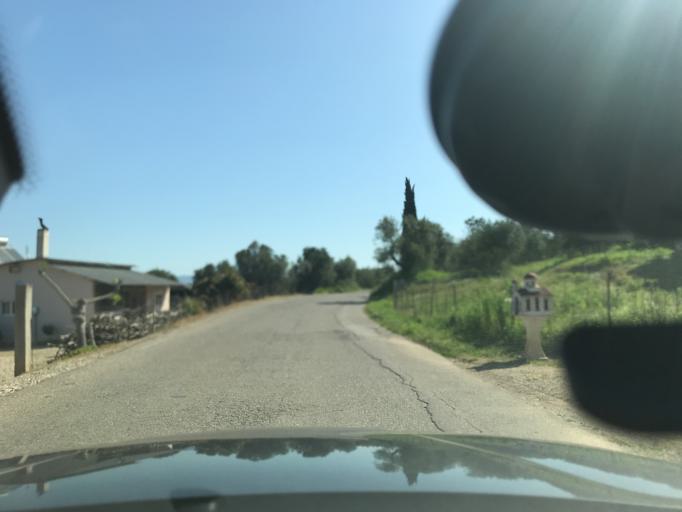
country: GR
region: West Greece
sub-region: Nomos Ileias
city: Alfiousa
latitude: 37.6411
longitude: 21.5187
